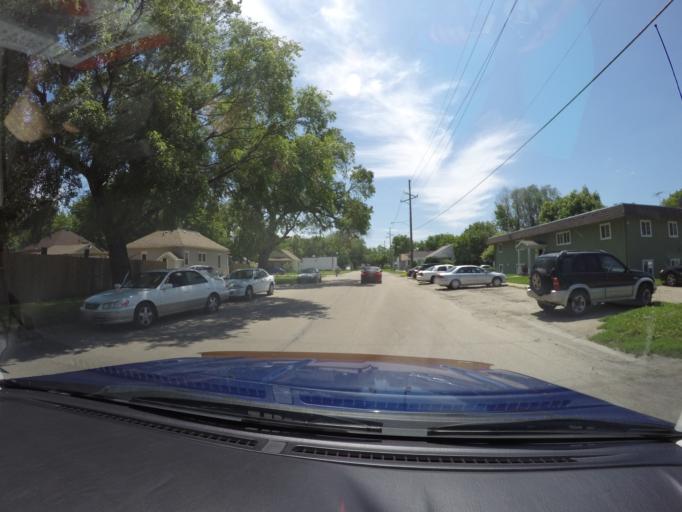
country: US
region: Nebraska
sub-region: Hall County
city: Grand Island
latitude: 40.9255
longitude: -98.3341
